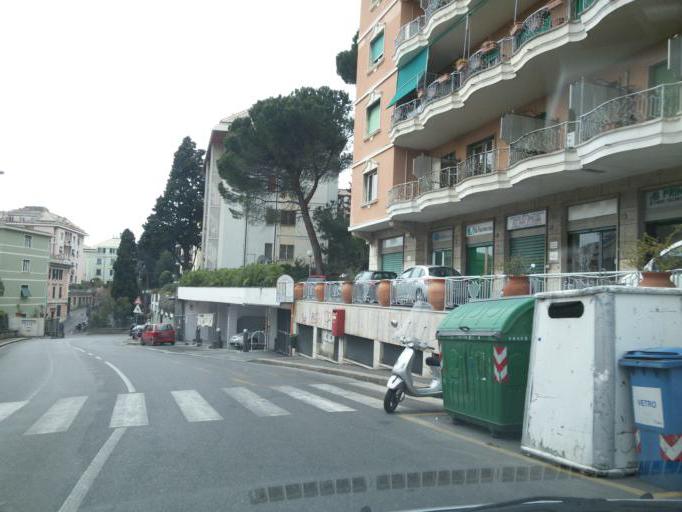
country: IT
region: Liguria
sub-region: Provincia di Genova
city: Genoa
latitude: 44.3999
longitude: 8.9790
